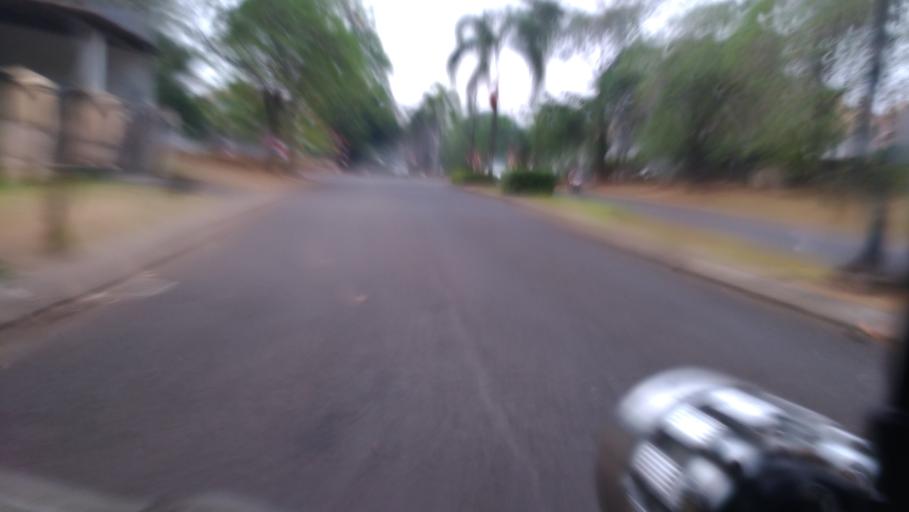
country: ID
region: West Java
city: Cileungsir
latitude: -6.4039
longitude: 106.9413
